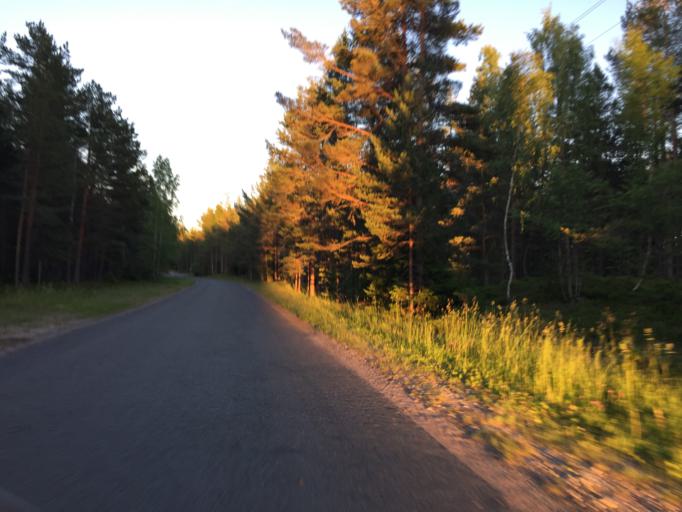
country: EE
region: Harju
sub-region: Kuusalu vald
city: Kuusalu
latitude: 59.5032
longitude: 25.2876
